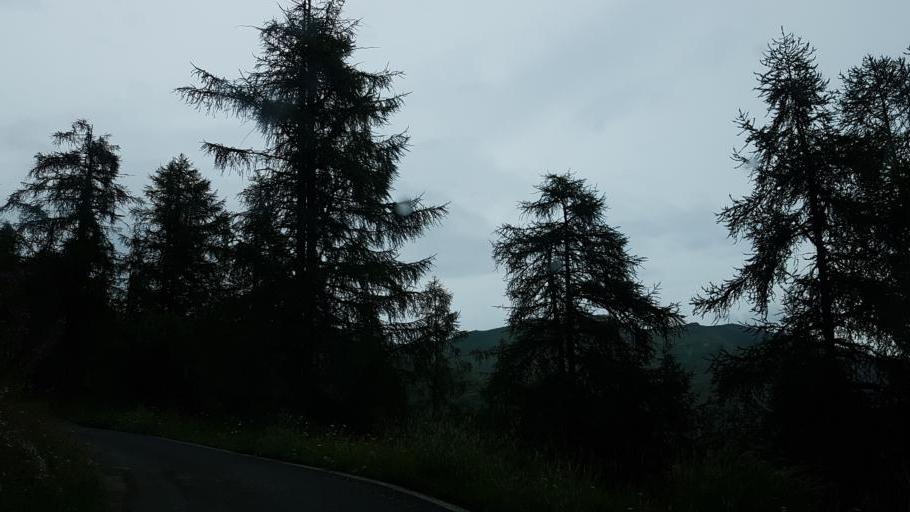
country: IT
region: Piedmont
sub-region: Provincia di Cuneo
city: Stroppo
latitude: 44.5151
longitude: 7.1051
